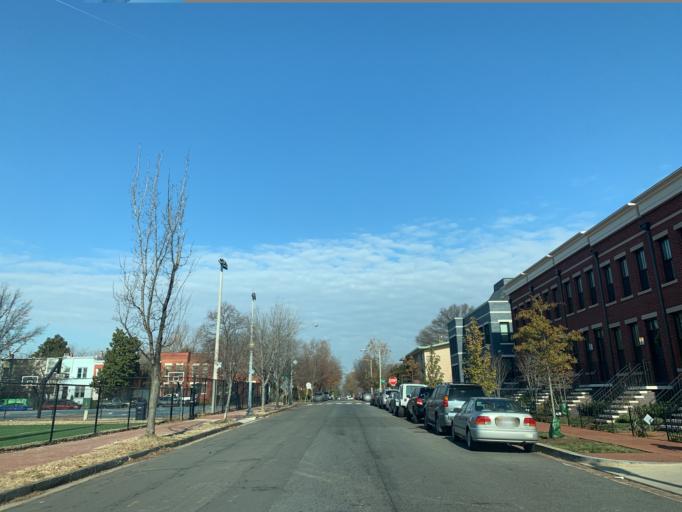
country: US
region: Washington, D.C.
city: Washington, D.C.
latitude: 38.8833
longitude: -76.9882
